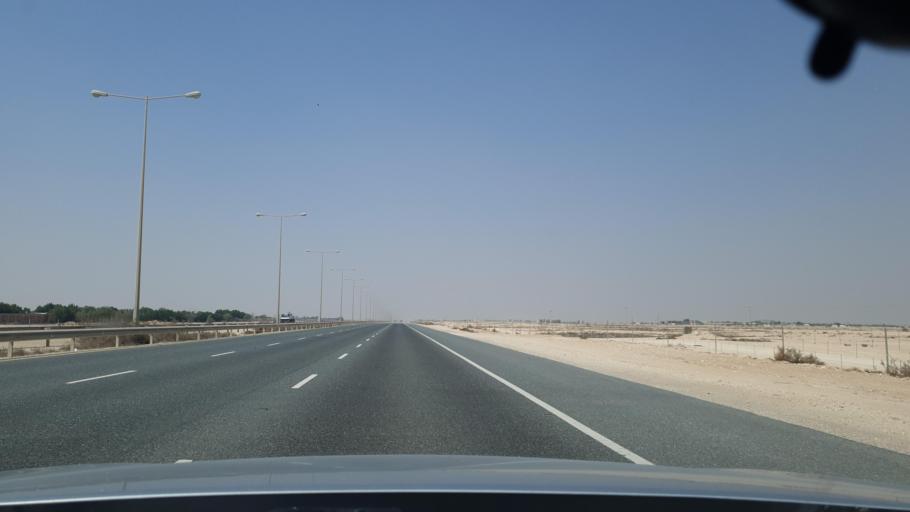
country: QA
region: Al Khawr
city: Al Khawr
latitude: 25.7625
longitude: 51.4223
